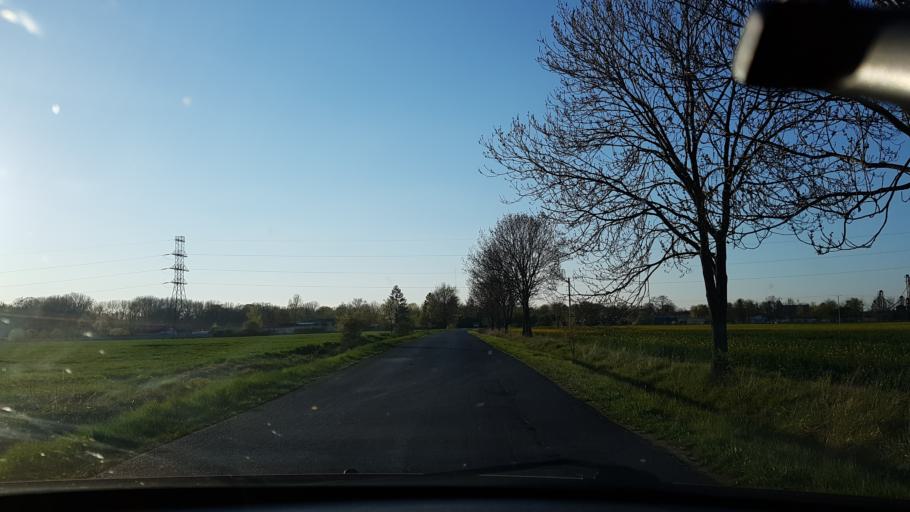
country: PL
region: Opole Voivodeship
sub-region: Powiat nyski
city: Nysa
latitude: 50.4262
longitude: 17.3100
